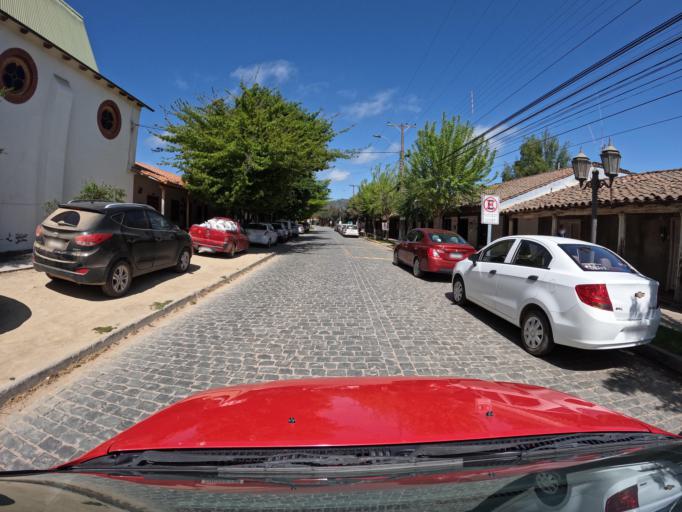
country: CL
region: O'Higgins
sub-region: Provincia de Colchagua
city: Santa Cruz
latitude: -34.7281
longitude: -71.6446
